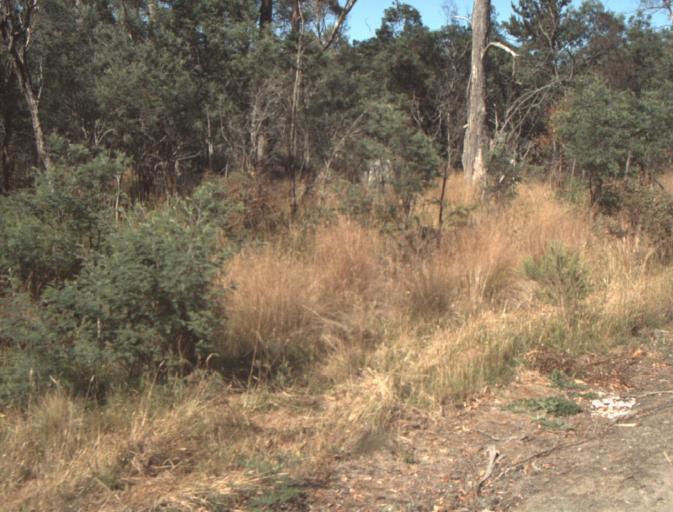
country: AU
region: Tasmania
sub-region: Launceston
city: Newstead
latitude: -41.3677
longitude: 147.2435
